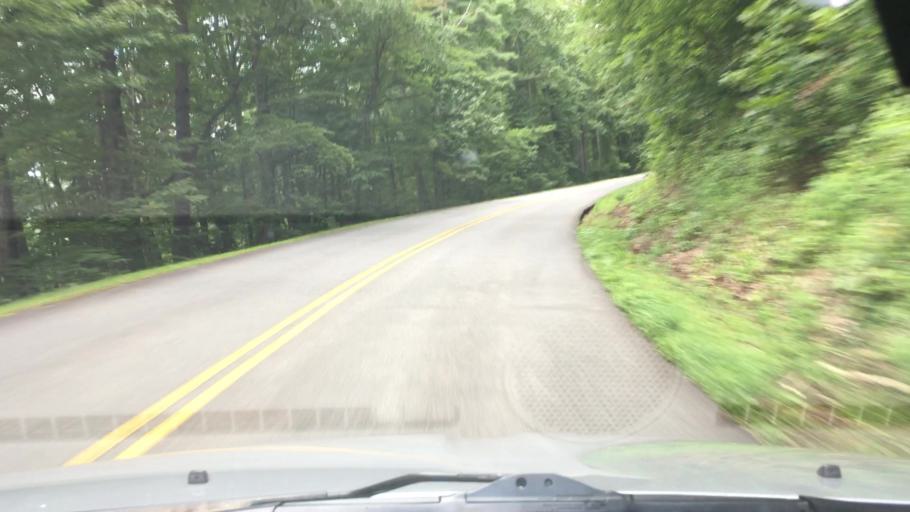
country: US
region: North Carolina
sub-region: Buncombe County
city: Asheville
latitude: 35.6070
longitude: -82.4935
